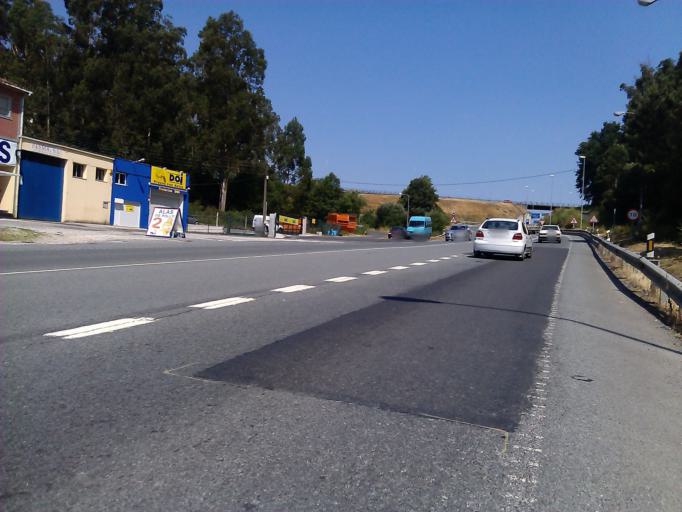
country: ES
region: Galicia
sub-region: Provincia da Coruna
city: Santiago de Compostela
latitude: 42.8530
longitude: -8.5283
